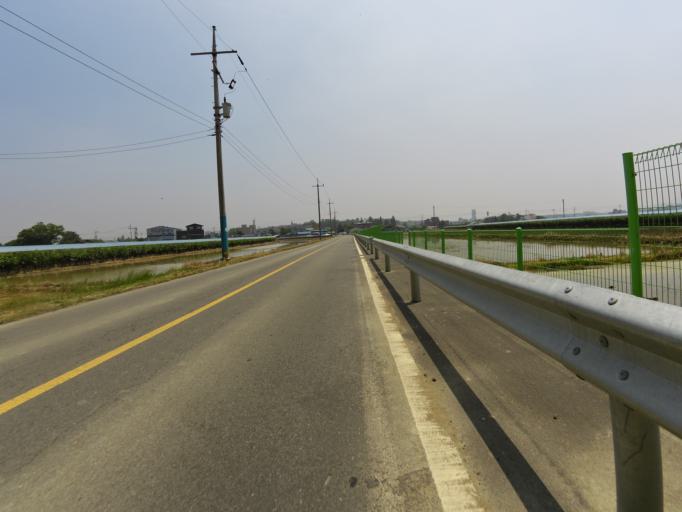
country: KR
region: Gyeongsangbuk-do
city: Gyeongsan-si
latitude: 35.8434
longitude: 128.7397
